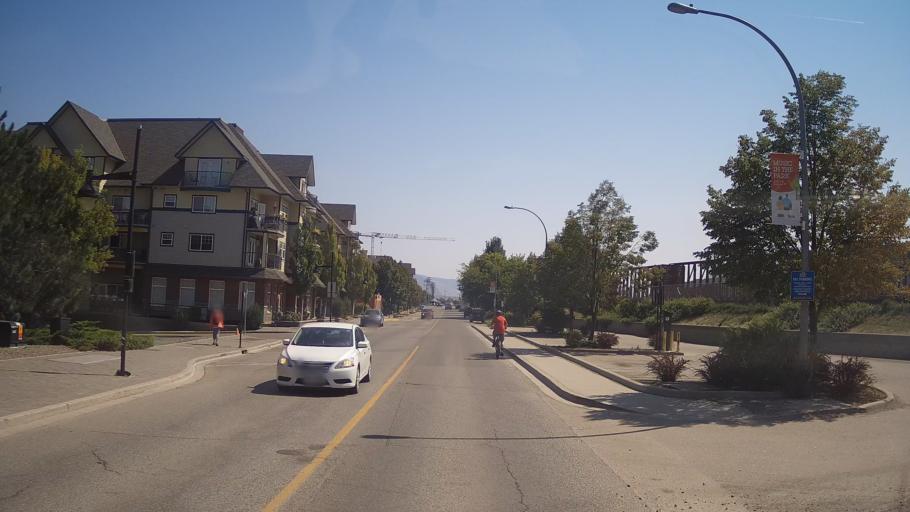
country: CA
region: British Columbia
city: Kamloops
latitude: 50.6781
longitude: -120.3323
